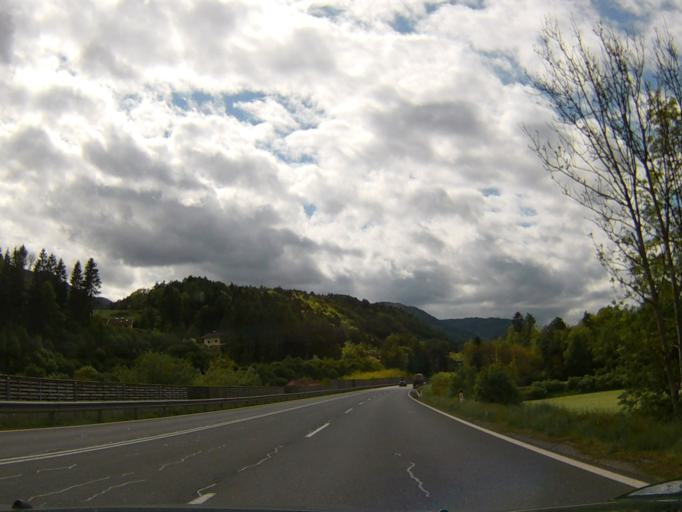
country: AT
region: Carinthia
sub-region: Politischer Bezirk Villach Land
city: Fresach
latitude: 46.6593
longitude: 13.7536
